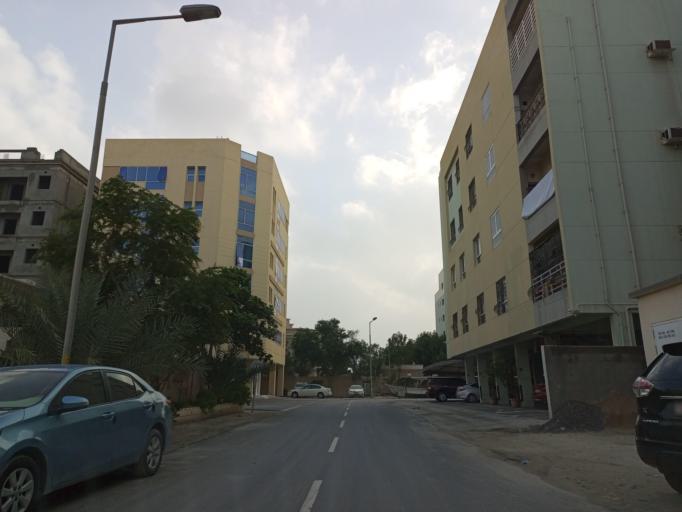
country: BH
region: Muharraq
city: Al Hadd
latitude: 26.2410
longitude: 50.6463
